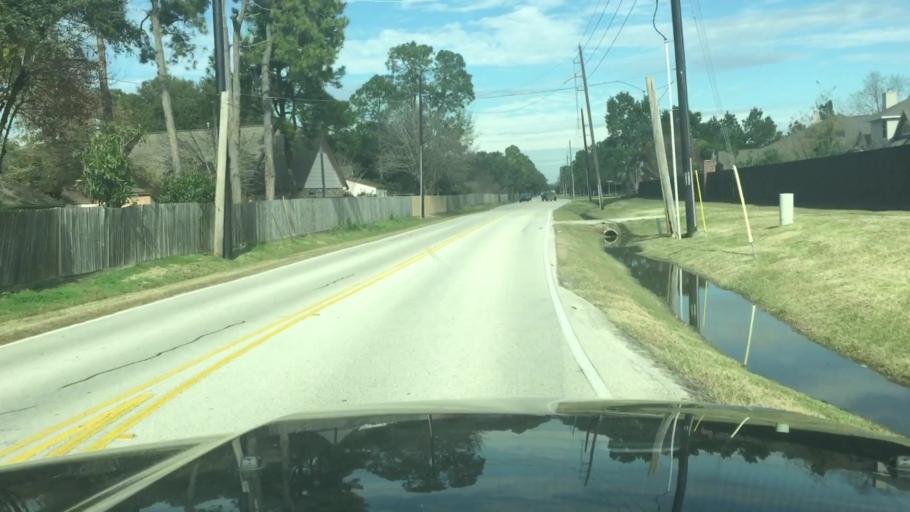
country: US
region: Texas
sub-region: Harris County
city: Oak Cliff Place
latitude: 29.8387
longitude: -95.6751
